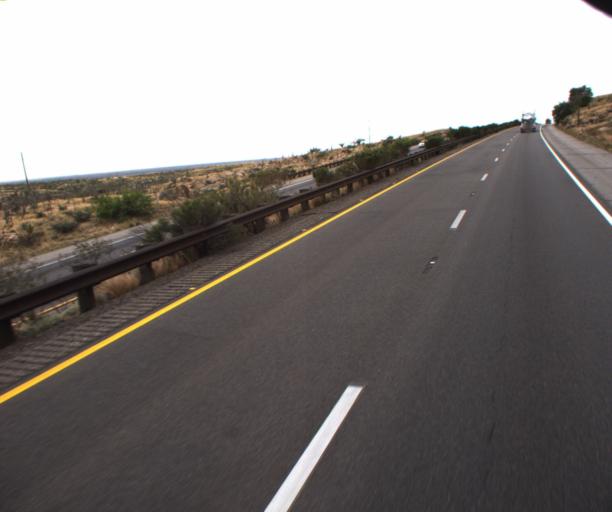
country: US
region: Arizona
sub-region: Cochise County
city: Saint David
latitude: 32.0188
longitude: -110.1142
